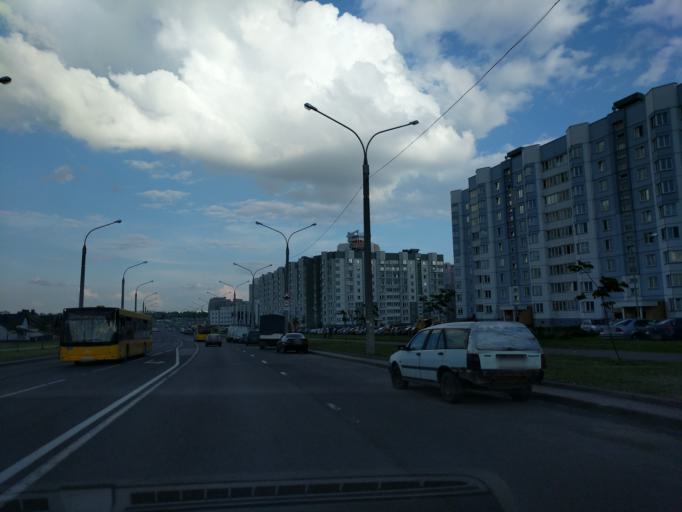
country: BY
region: Minsk
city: Zhdanovichy
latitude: 53.9342
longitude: 27.4353
